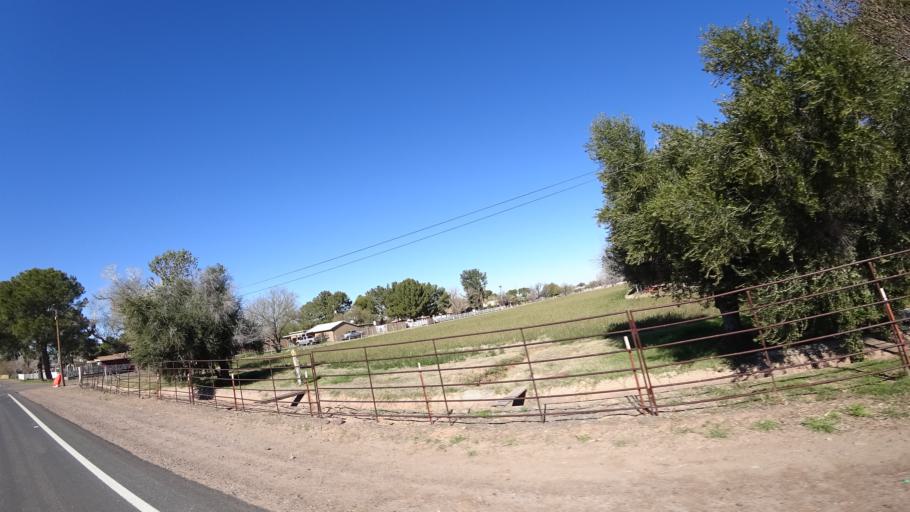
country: US
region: Arizona
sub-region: Maricopa County
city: Tolleson
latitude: 33.3919
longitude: -112.2927
